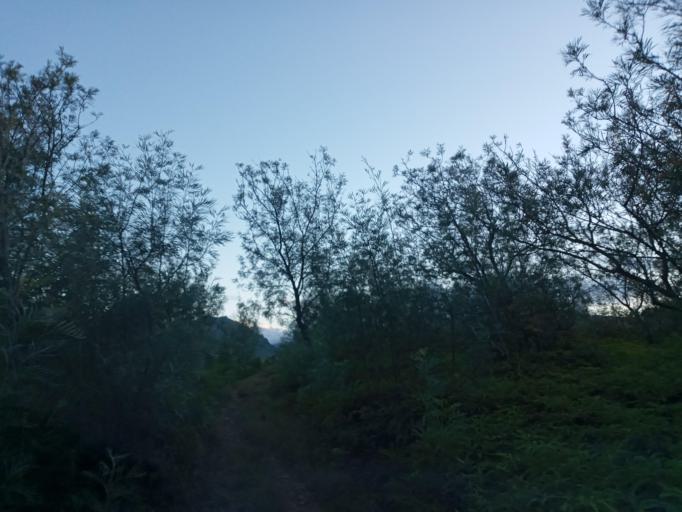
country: MG
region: Anosy
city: Fort Dauphin
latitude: -24.5116
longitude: 47.2225
